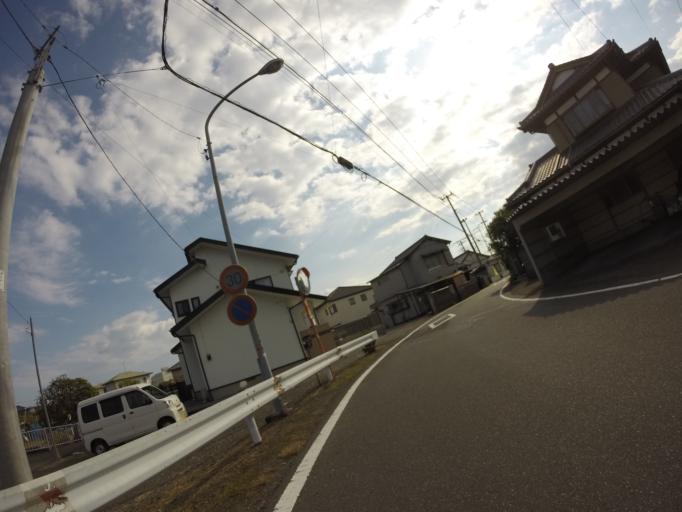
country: JP
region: Shizuoka
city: Fuji
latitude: 35.1612
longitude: 138.6342
